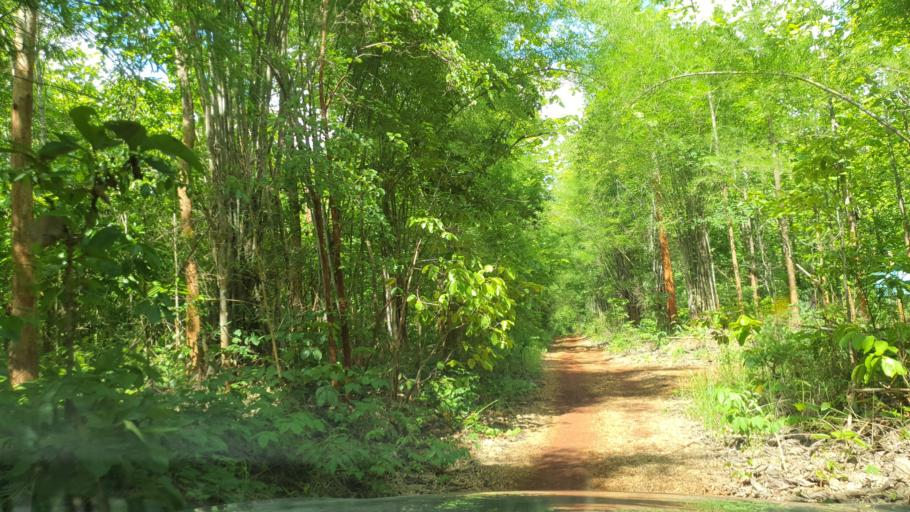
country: TH
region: Chiang Mai
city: Mae Taeng
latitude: 19.0795
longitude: 99.0893
